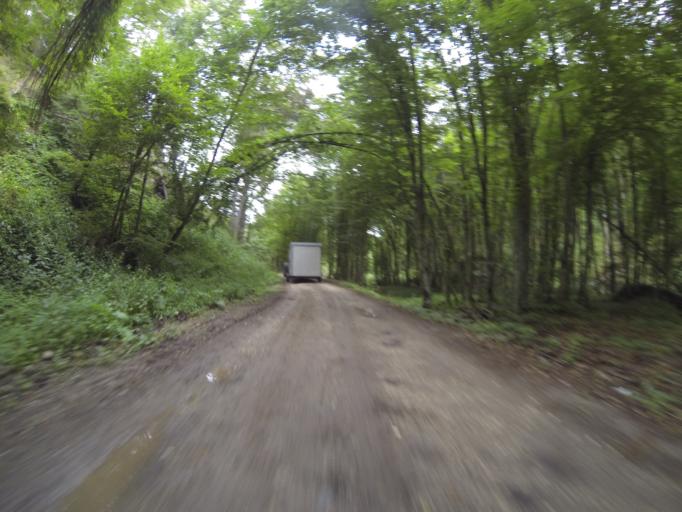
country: RO
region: Brasov
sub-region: Comuna Sinca Veche
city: Sinca Veche
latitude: 45.6897
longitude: 25.1554
